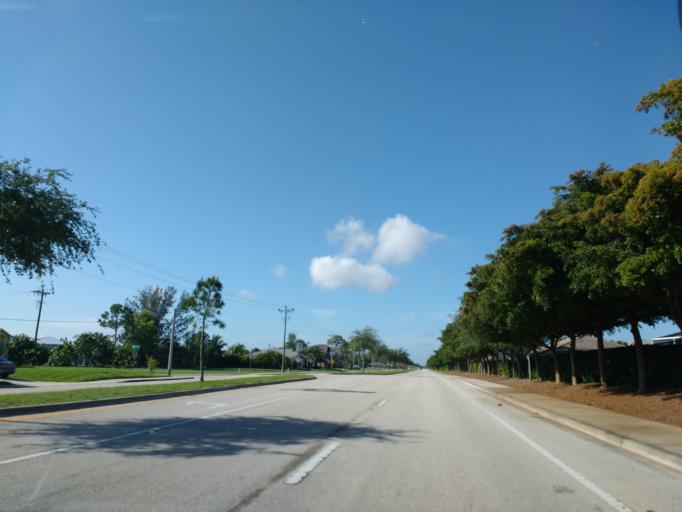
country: US
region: Florida
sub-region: Lee County
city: Cape Coral
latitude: 26.6187
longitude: -82.0234
